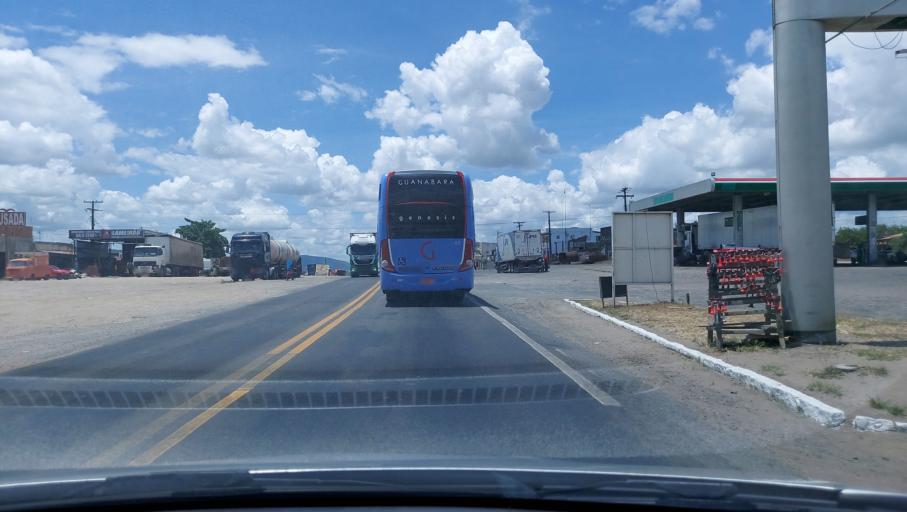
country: BR
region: Bahia
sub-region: Castro Alves
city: Castro Alves
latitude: -12.5816
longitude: -39.5183
